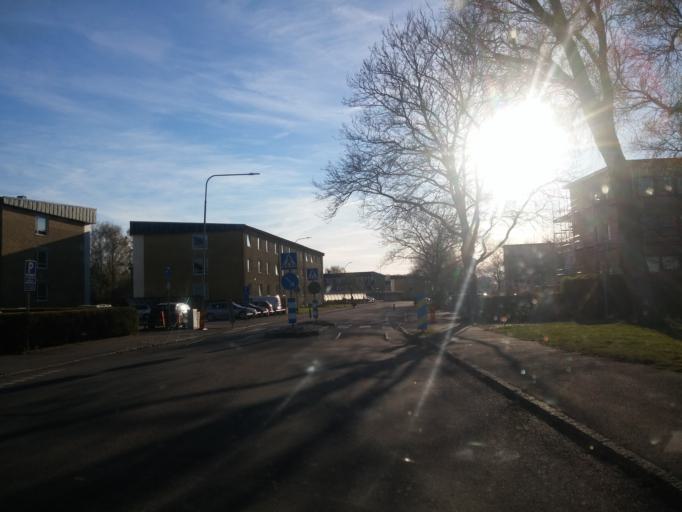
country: SE
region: Skane
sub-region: Angelholms Kommun
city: AEngelholm
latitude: 56.2502
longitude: 12.8802
